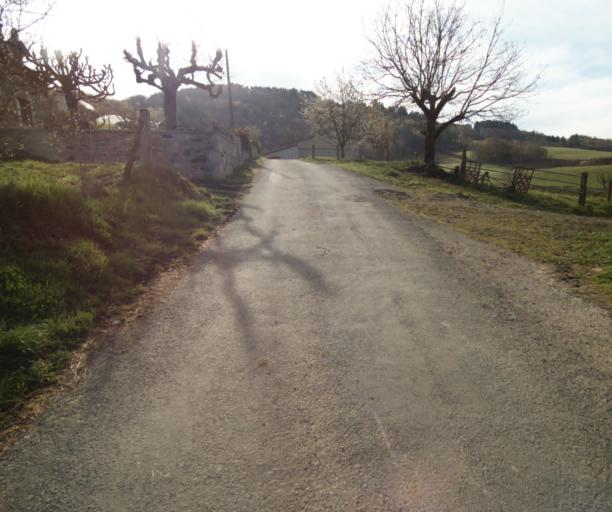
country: FR
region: Limousin
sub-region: Departement de la Correze
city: Naves
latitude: 45.3418
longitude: 1.8196
